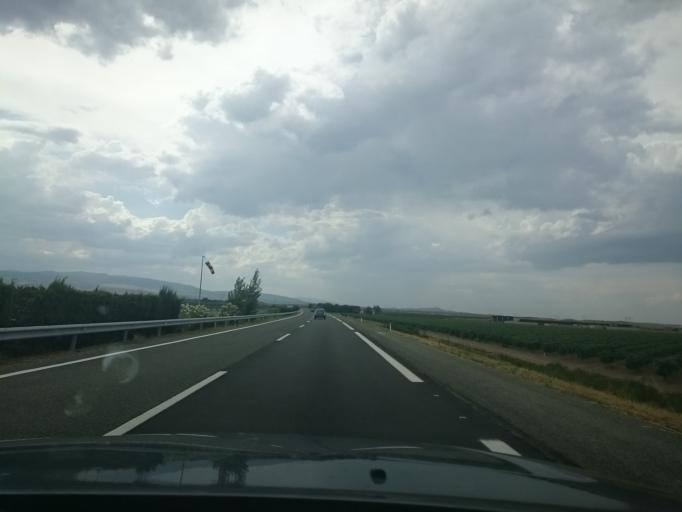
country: ES
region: Navarre
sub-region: Provincia de Navarra
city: Corella
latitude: 42.1501
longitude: -1.7944
